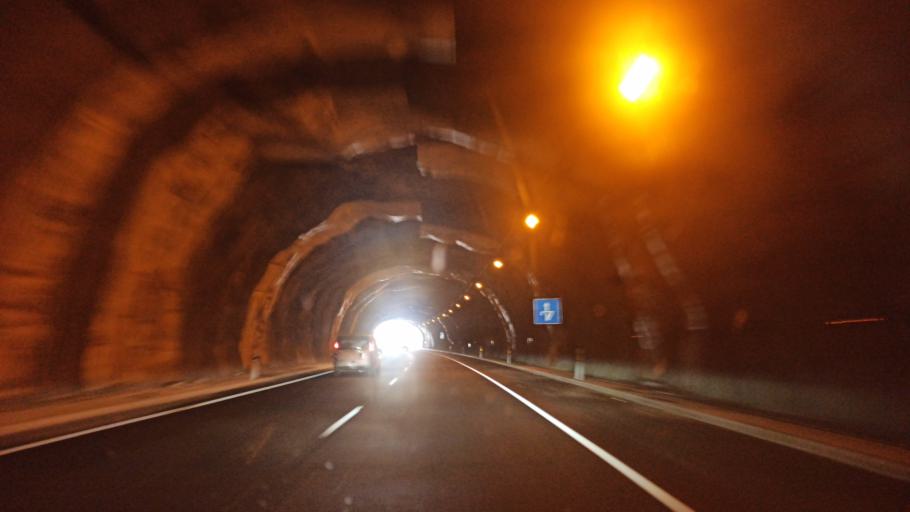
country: ES
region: Catalonia
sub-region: Provincia de Barcelona
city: Sant Pere de Ribes
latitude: 41.2838
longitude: 1.7289
